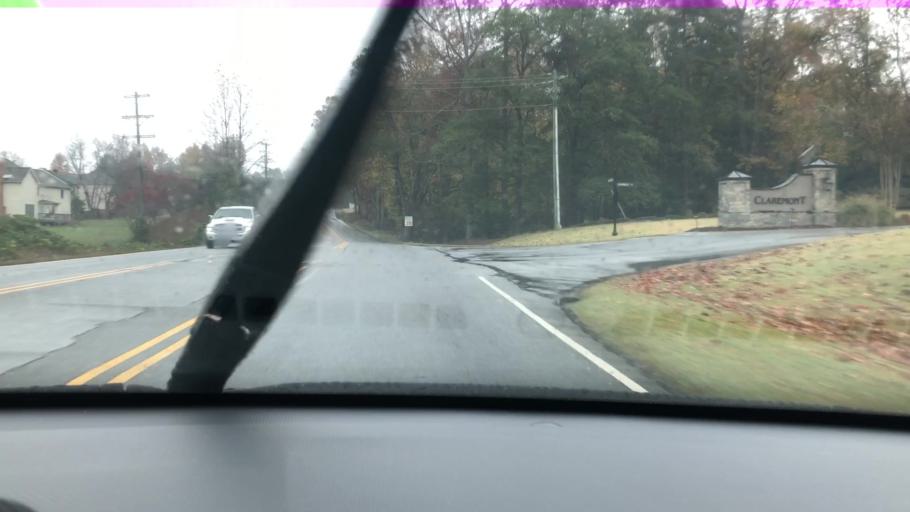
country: US
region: South Carolina
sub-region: Greenville County
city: Five Forks
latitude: 34.8300
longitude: -82.2629
